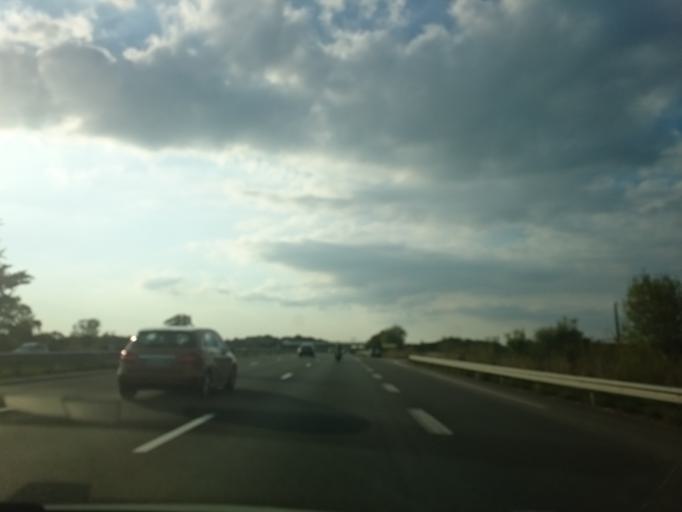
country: FR
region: Pays de la Loire
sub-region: Departement de la Loire-Atlantique
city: Malville
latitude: 47.3544
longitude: -1.8878
